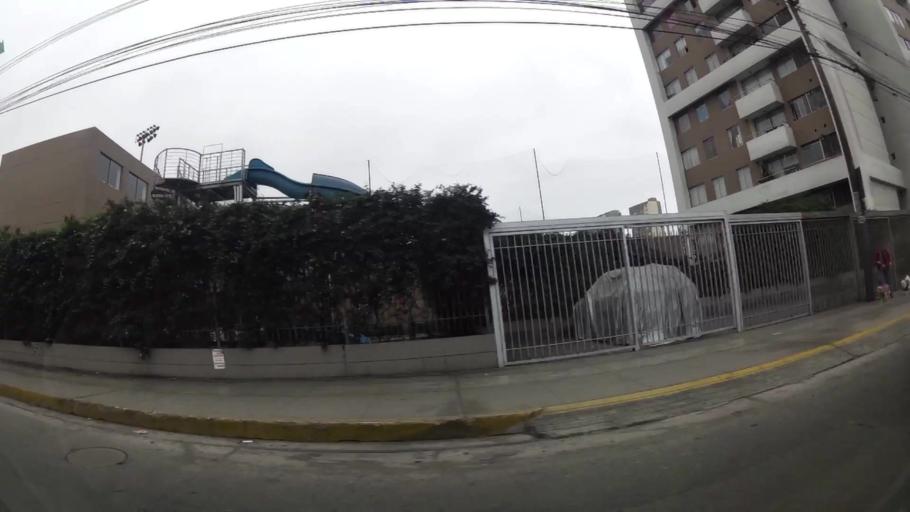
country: PE
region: Callao
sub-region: Callao
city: Callao
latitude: -12.0736
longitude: -77.0786
